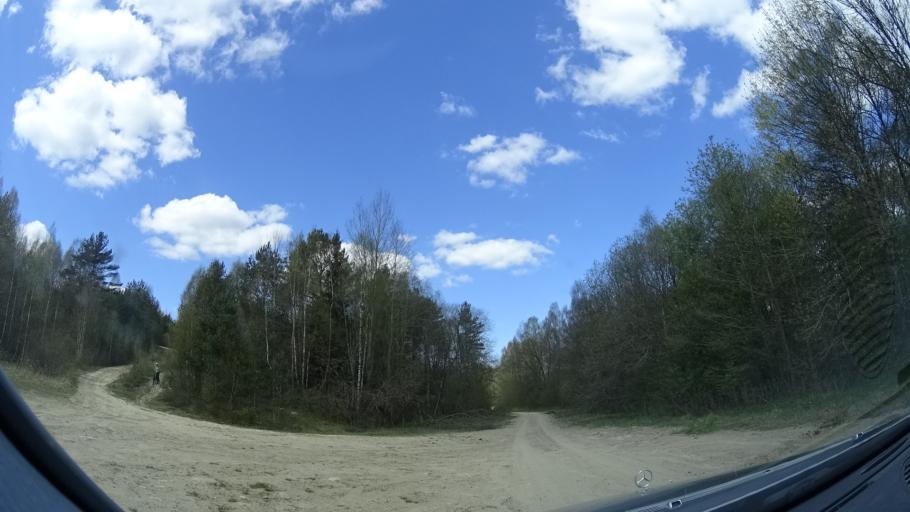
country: SE
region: Skane
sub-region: Hassleholms Kommun
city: Tormestorp
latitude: 56.0944
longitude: 13.7174
